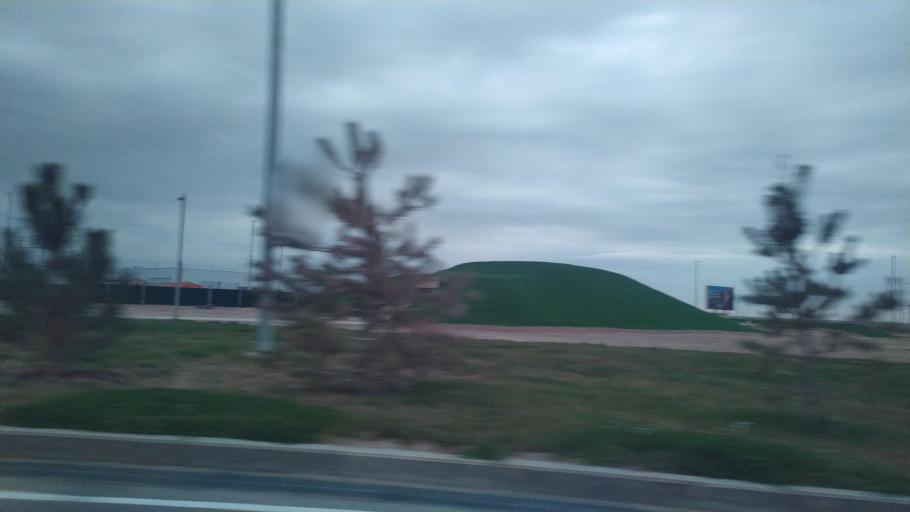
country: KZ
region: Ongtustik Qazaqstan
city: Kentau
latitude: 43.3162
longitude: 68.5454
